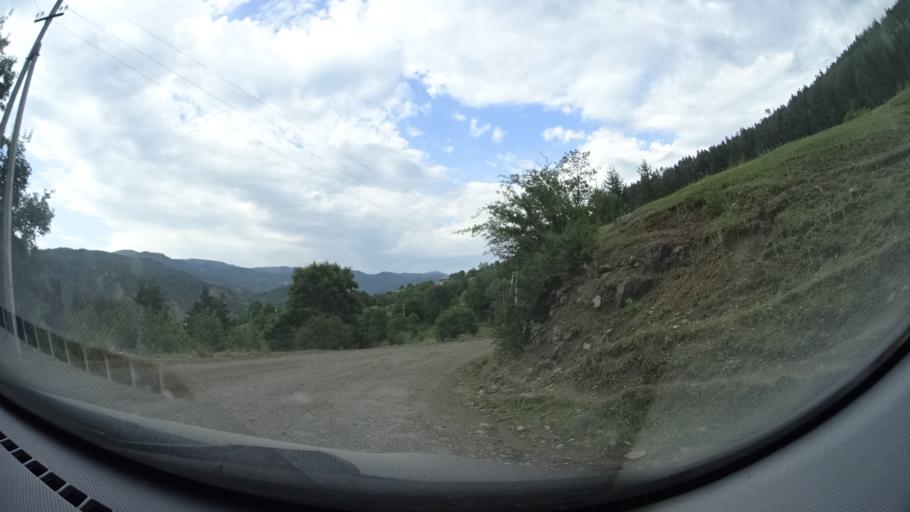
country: GE
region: Samtskhe-Javakheti
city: Adigeni
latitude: 41.6754
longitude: 42.6447
